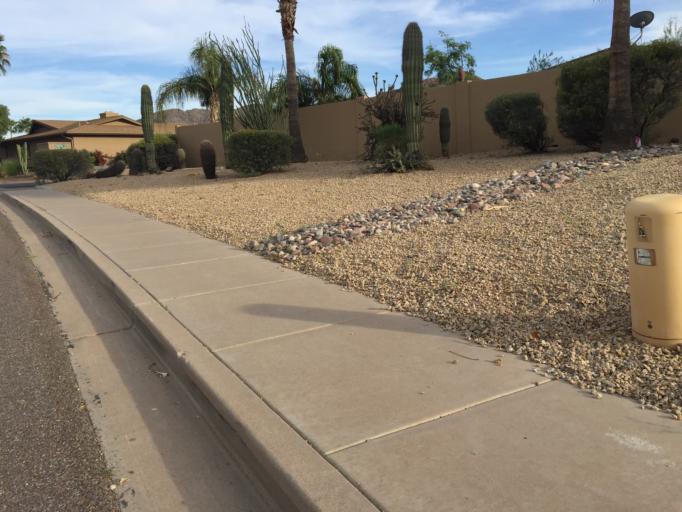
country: US
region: Arizona
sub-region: Maricopa County
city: Paradise Valley
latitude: 33.5702
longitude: -112.0140
